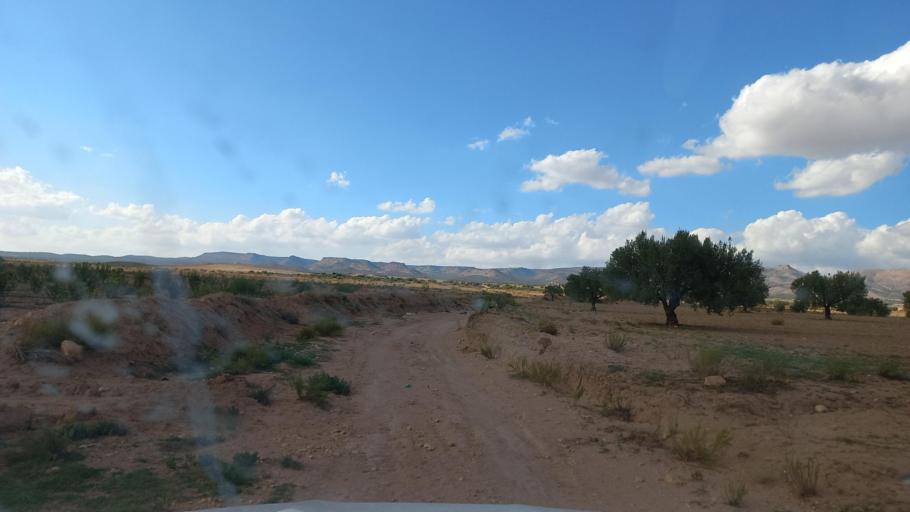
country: TN
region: Al Qasrayn
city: Sbiba
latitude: 35.3934
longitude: 9.0367
